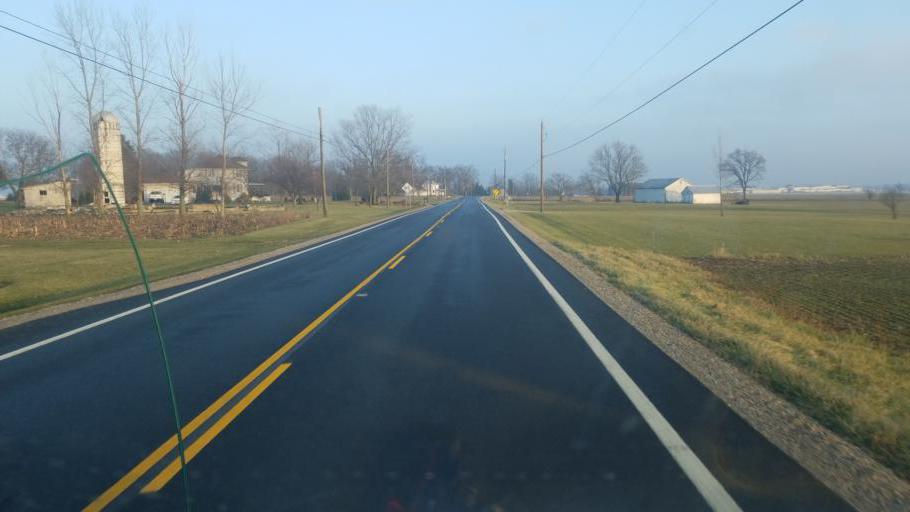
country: US
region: Ohio
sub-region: Wyandot County
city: Carey
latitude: 40.9614
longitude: -83.4180
